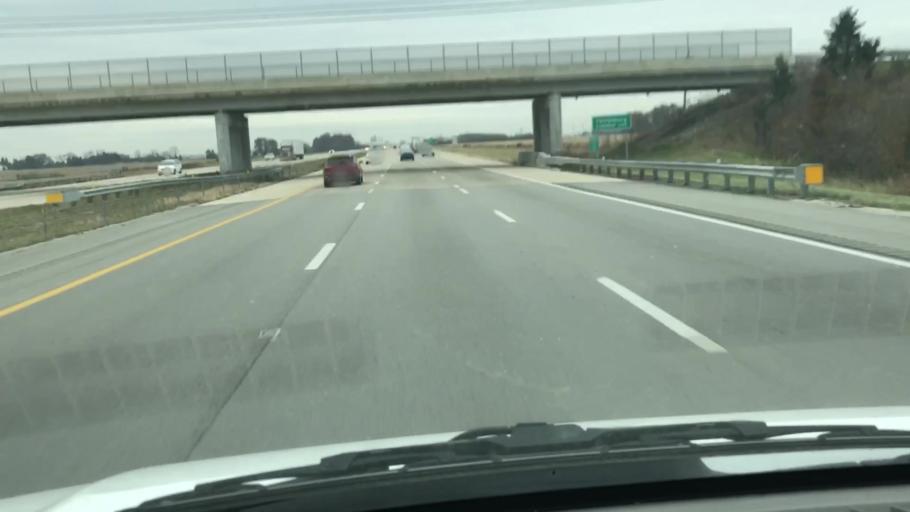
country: US
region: Ohio
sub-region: Wood County
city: Perrysburg
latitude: 41.5226
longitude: -83.6220
